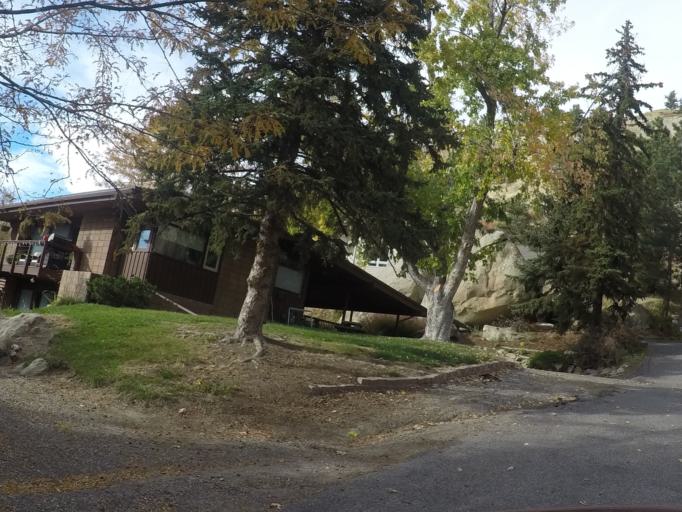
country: US
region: Montana
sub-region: Yellowstone County
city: Billings
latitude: 45.8012
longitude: -108.5552
